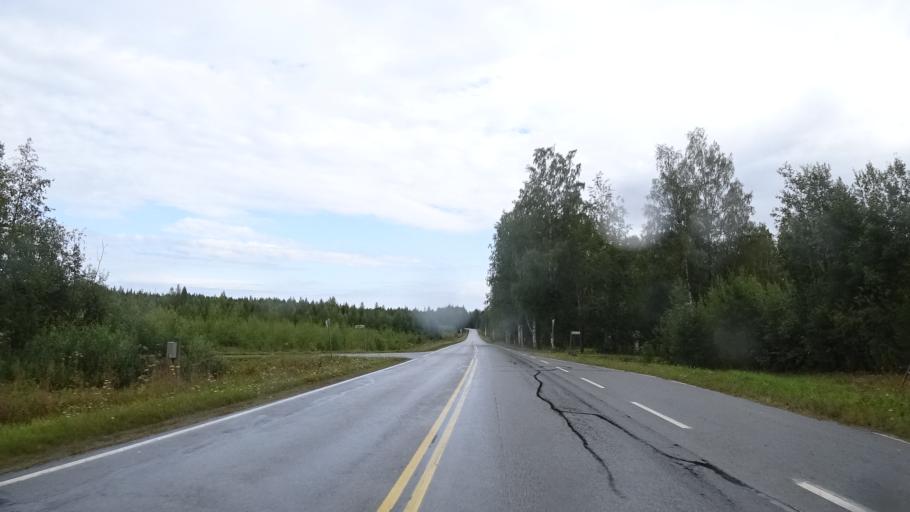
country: FI
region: North Karelia
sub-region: Keski-Karjala
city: Raeaekkylae
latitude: 62.0786
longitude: 29.6523
